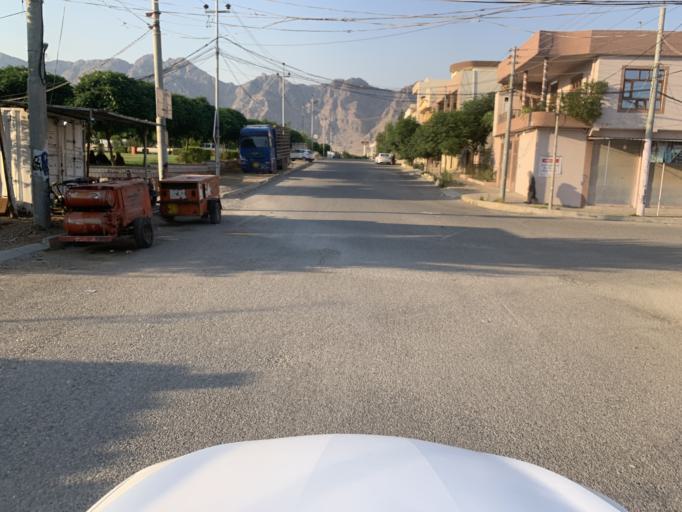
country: IQ
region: As Sulaymaniyah
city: Raniye
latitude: 36.2437
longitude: 44.8802
